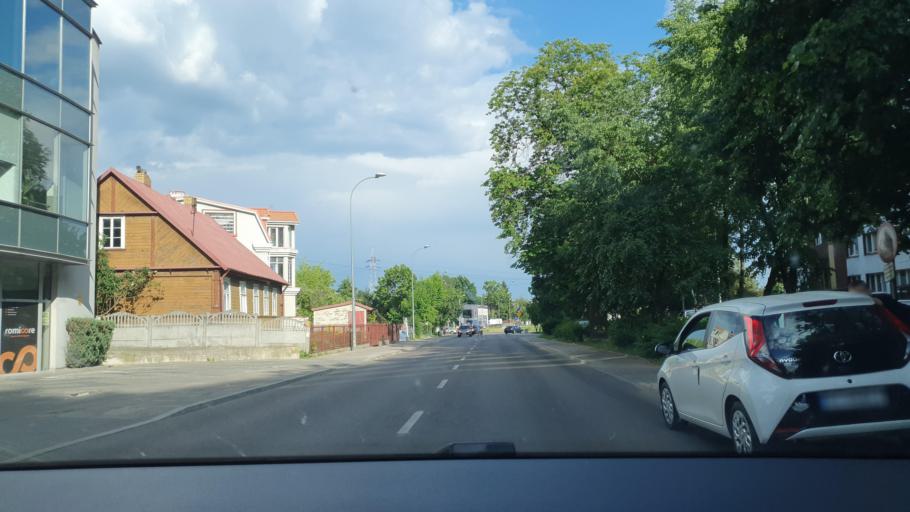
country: PL
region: Podlasie
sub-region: Bialystok
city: Bialystok
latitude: 53.1274
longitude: 23.1816
